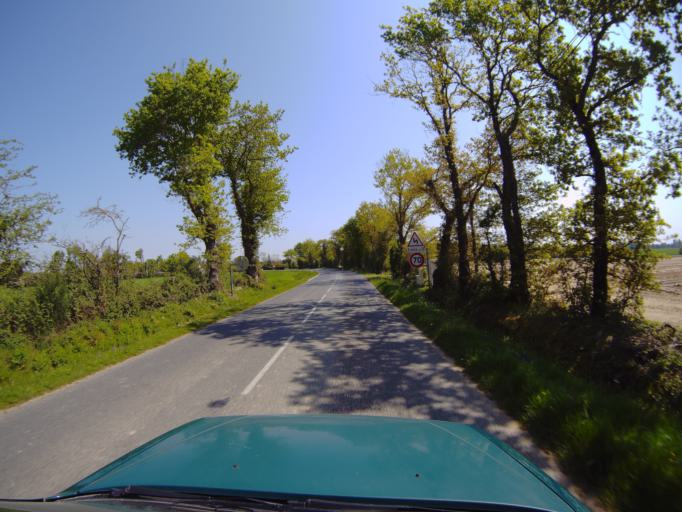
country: FR
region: Pays de la Loire
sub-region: Departement de la Vendee
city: Saint-Andre-Treize-Voies
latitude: 46.9417
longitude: -1.3816
